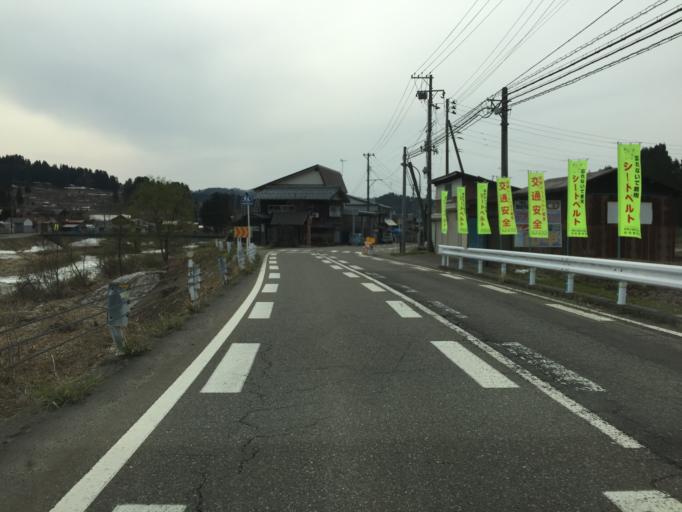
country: JP
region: Niigata
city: Tochio-honcho
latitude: 37.4444
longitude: 139.0284
